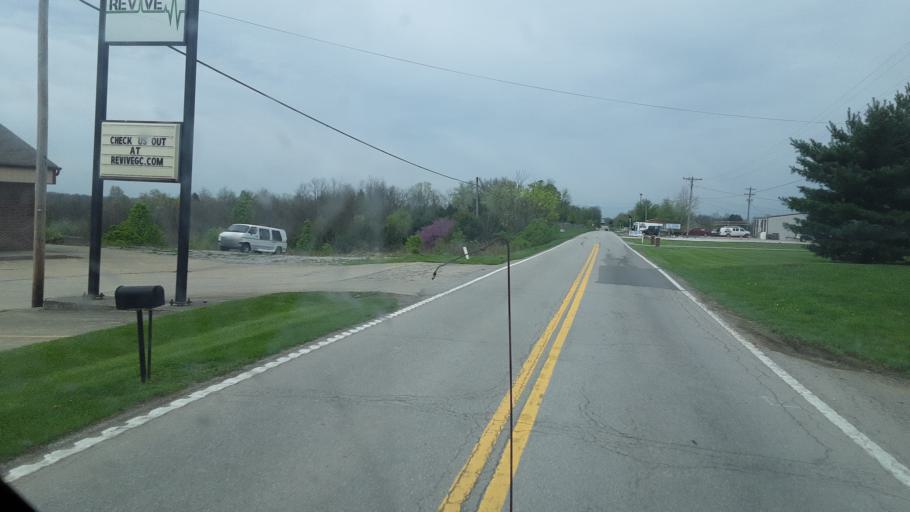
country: US
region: Kentucky
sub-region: Grant County
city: Dry Ridge
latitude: 38.6767
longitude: -84.6280
